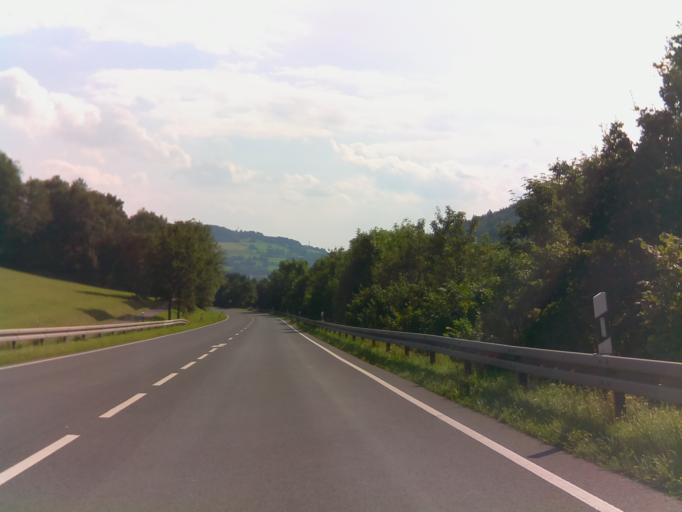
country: DE
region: Bavaria
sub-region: Regierungsbezirk Unterfranken
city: Riedenberg
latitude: 50.3428
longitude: 9.8814
